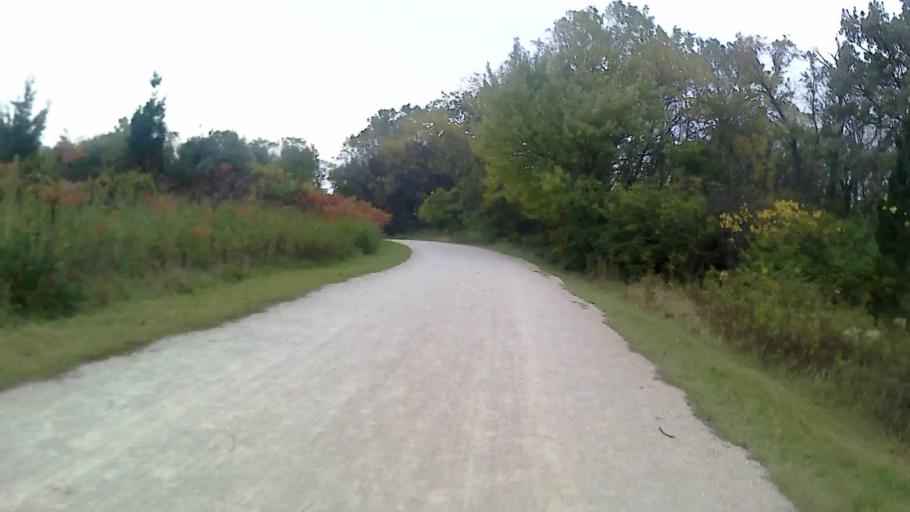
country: US
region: Illinois
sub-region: DuPage County
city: Naperville
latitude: 41.8116
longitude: -88.1423
